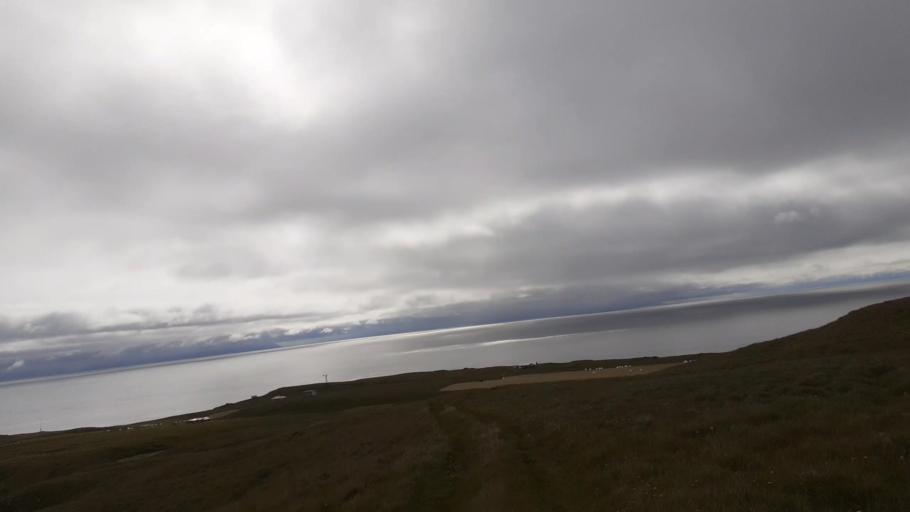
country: IS
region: Northeast
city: Dalvik
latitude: 66.5352
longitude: -17.9821
